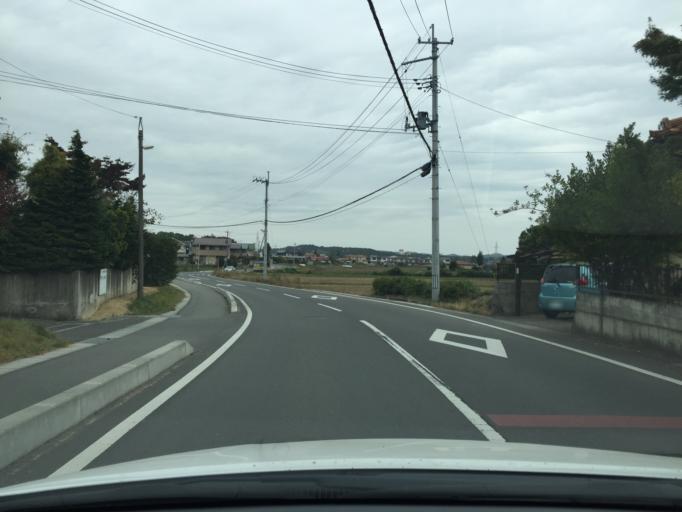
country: JP
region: Tochigi
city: Kuroiso
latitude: 37.1325
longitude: 140.1474
